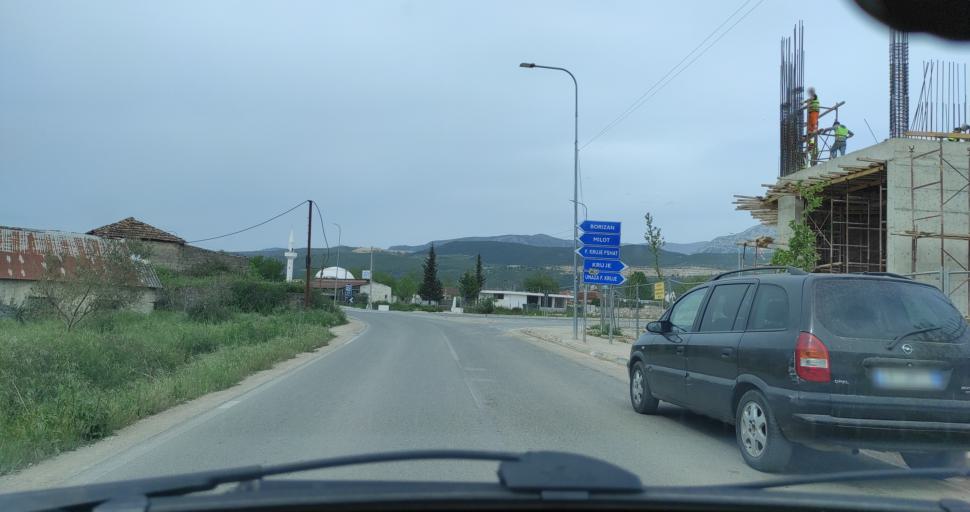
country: AL
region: Durres
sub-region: Rrethi i Krujes
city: Fushe-Kruje
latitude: 41.4863
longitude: 19.7259
